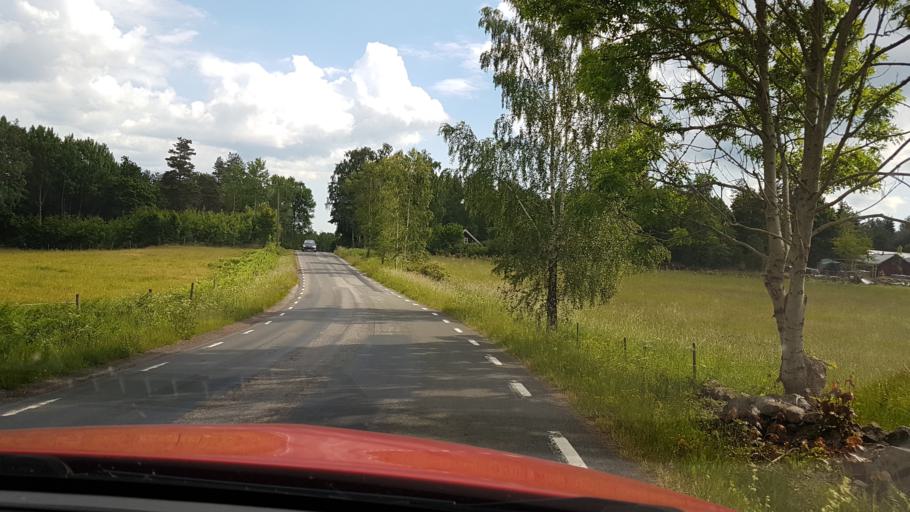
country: SE
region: Vaestra Goetaland
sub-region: Tibro Kommun
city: Tibro
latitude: 58.3126
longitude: 14.1696
